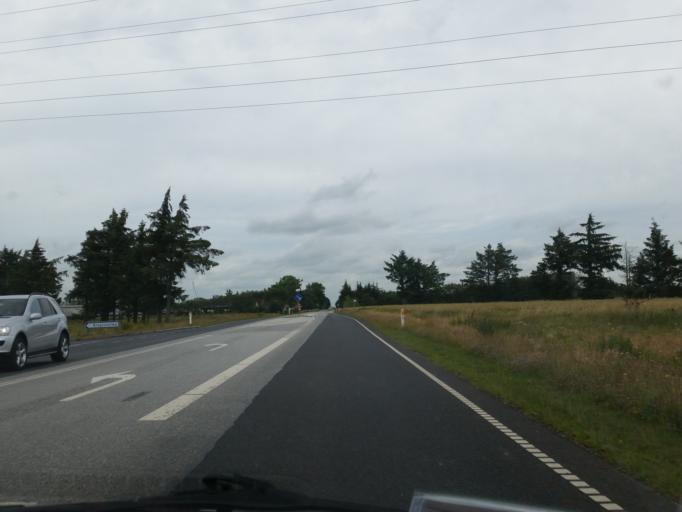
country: DK
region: South Denmark
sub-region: Esbjerg Kommune
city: Ribe
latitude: 55.3565
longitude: 8.7903
